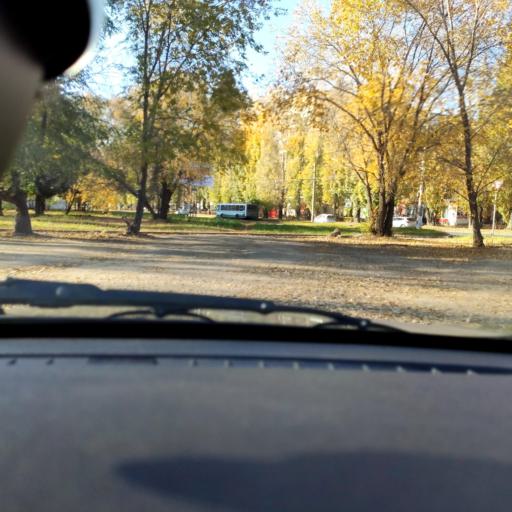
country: RU
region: Samara
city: Tol'yatti
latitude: 53.5091
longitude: 49.4271
